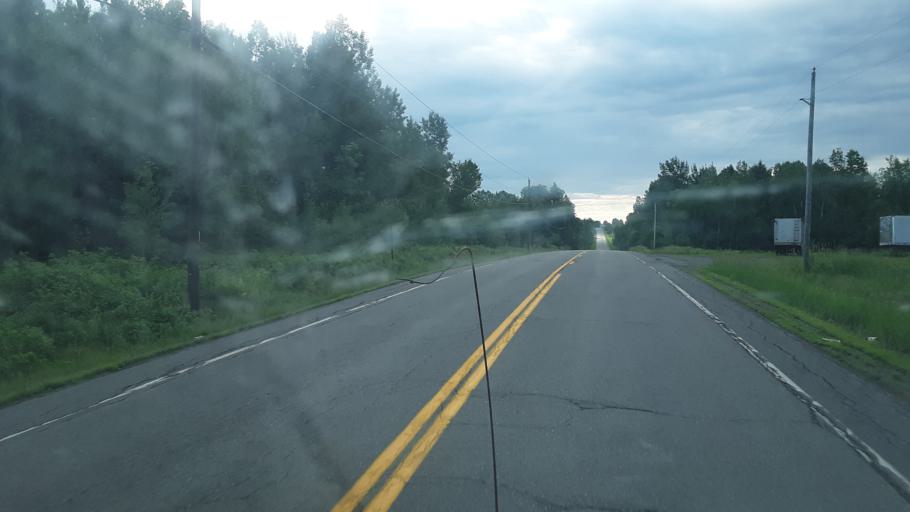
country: US
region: Maine
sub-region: Penobscot County
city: Patten
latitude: 45.8709
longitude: -68.3471
